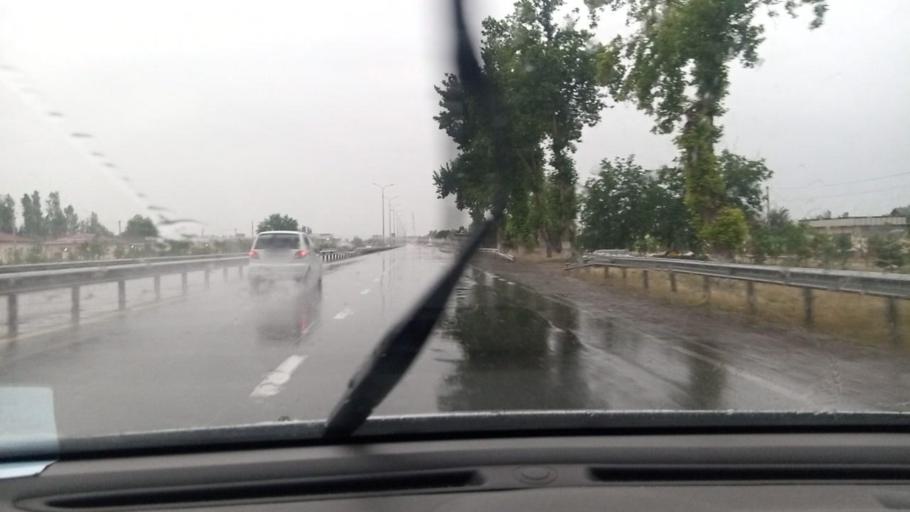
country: UZ
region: Toshkent Shahri
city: Bektemir
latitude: 41.1349
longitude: 69.4349
